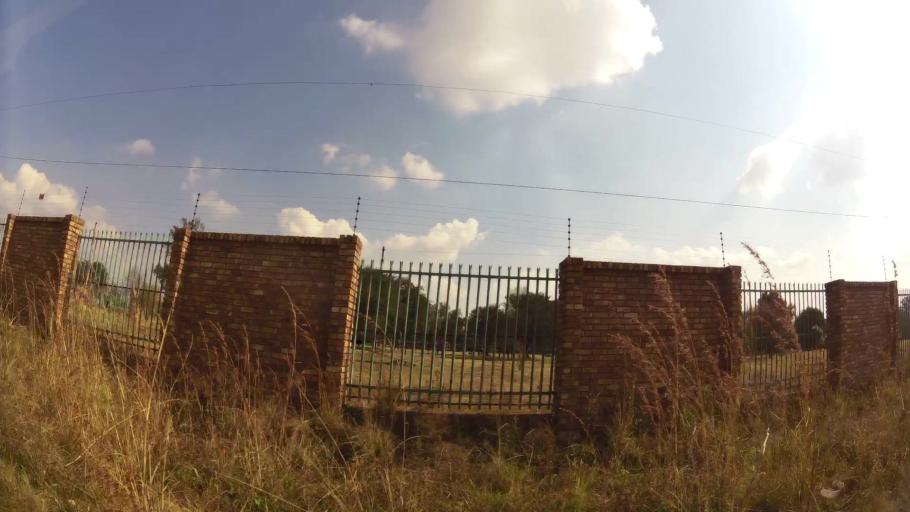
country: ZA
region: Mpumalanga
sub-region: Nkangala District Municipality
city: Delmas
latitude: -26.1843
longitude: 28.5402
